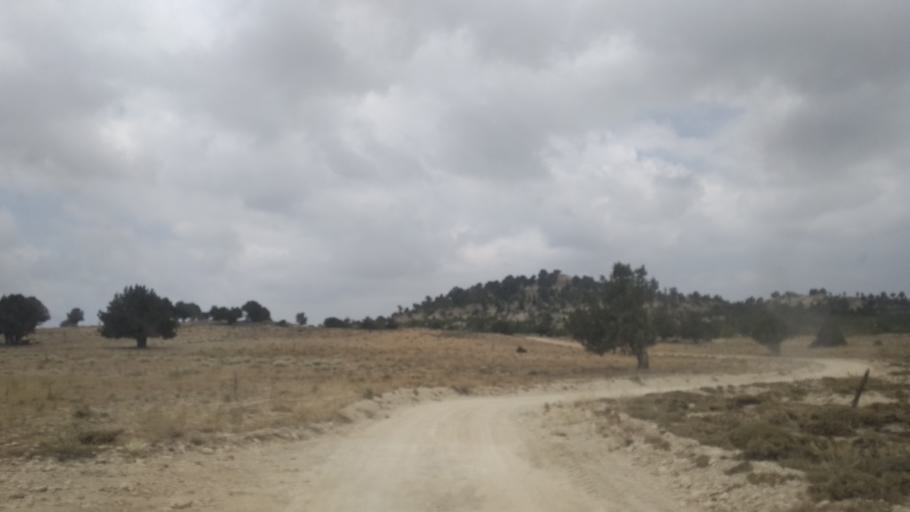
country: TR
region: Mersin
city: Sarikavak
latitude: 36.5744
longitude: 33.7579
